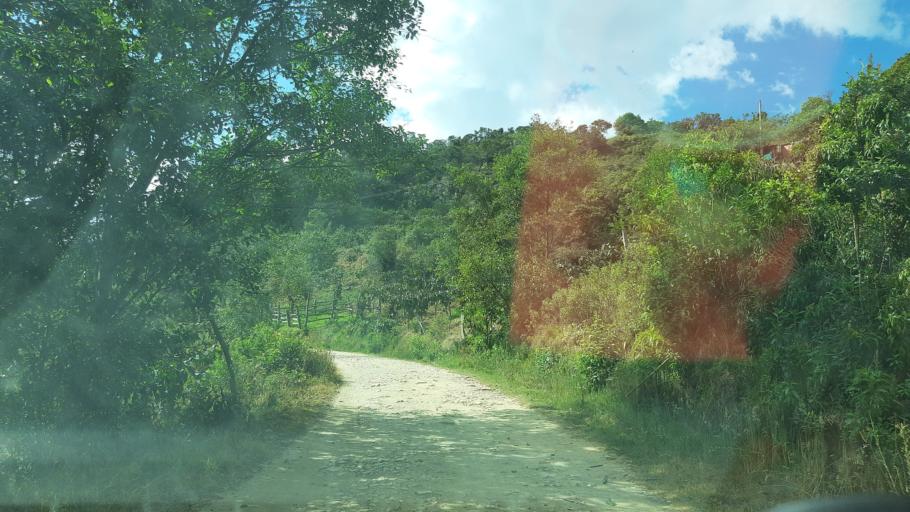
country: CO
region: Boyaca
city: Santa Sofia
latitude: 5.7319
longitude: -73.5528
